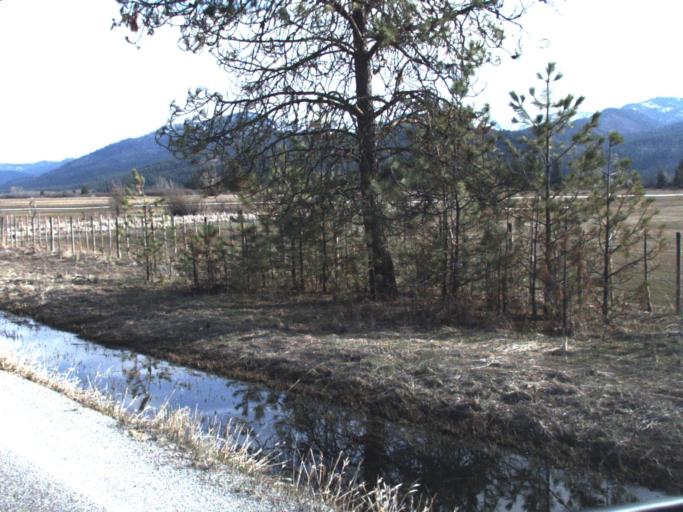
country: US
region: Washington
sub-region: Pend Oreille County
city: Newport
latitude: 48.3692
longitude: -117.3047
